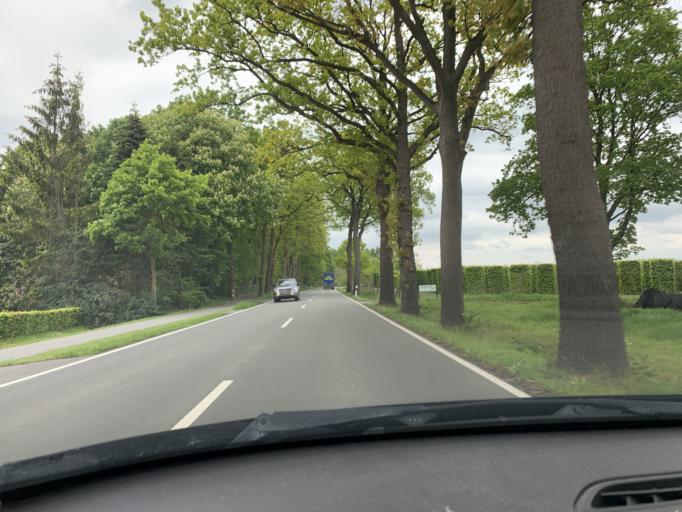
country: DE
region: Lower Saxony
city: Bad Zwischenahn
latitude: 53.2010
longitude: 8.0431
